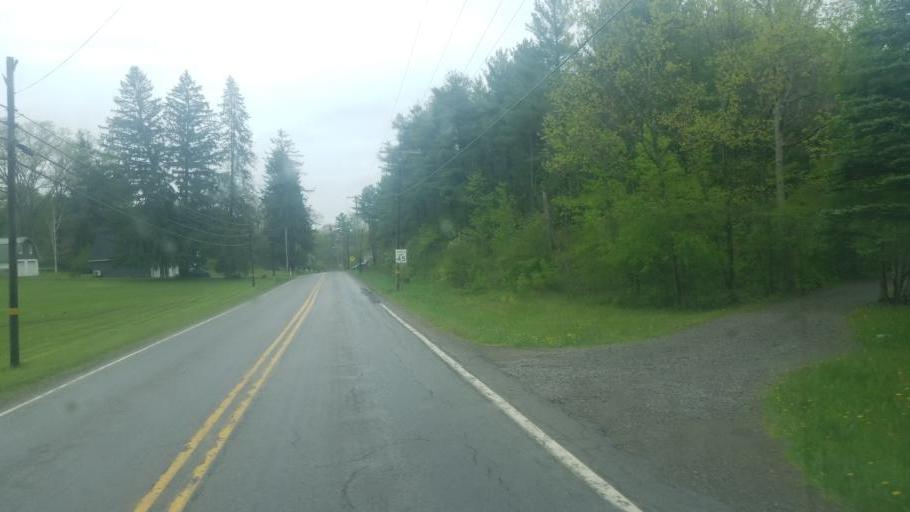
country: US
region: Pennsylvania
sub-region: Clarion County
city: Marianne
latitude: 41.3744
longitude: -79.3091
